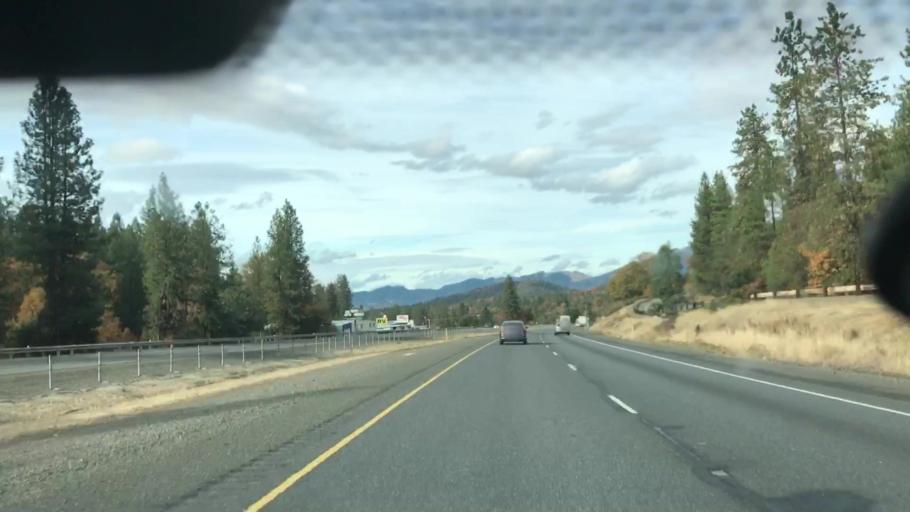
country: US
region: Oregon
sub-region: Josephine County
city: Grants Pass
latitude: 42.4890
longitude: -123.3620
